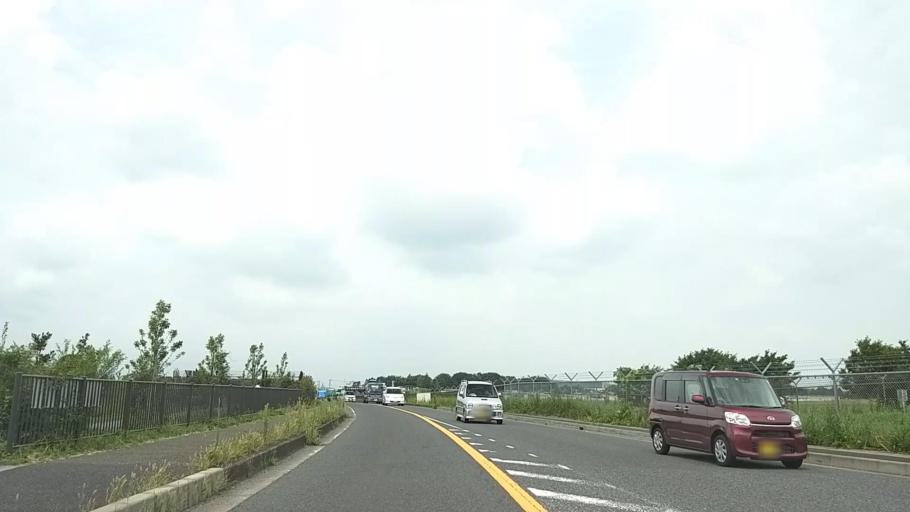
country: JP
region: Kanagawa
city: Minami-rinkan
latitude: 35.4396
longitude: 139.4526
